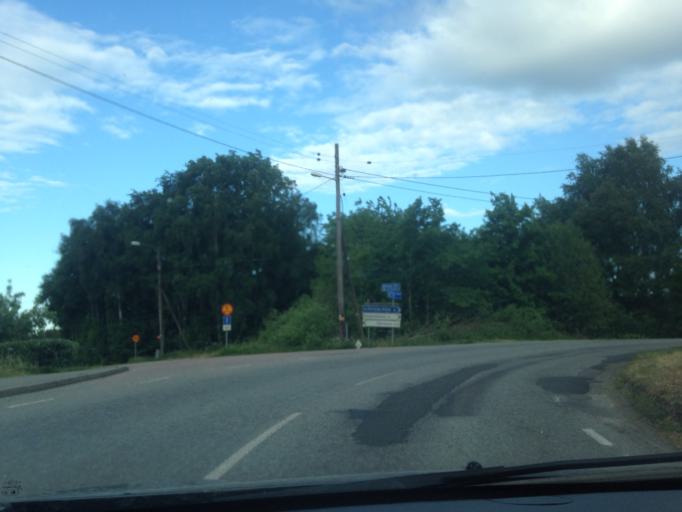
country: SE
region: Vaestra Goetaland
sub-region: Goteborg
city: Torslanda
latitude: 57.7627
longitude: 11.8323
